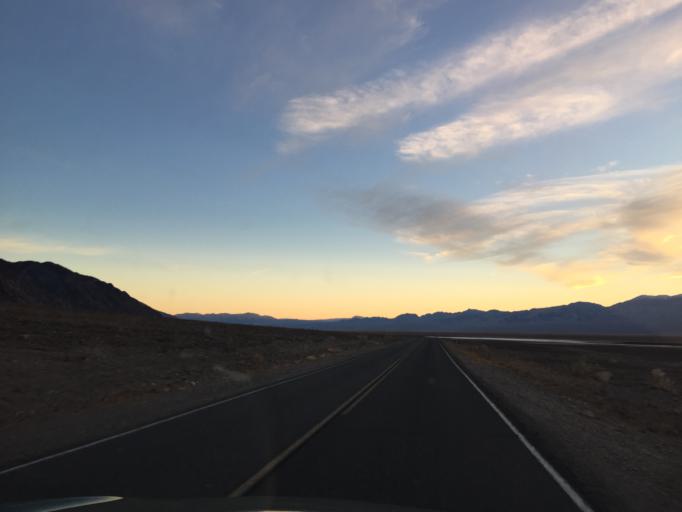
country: US
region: Nevada
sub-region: Nye County
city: Beatty
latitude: 36.2099
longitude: -116.7759
